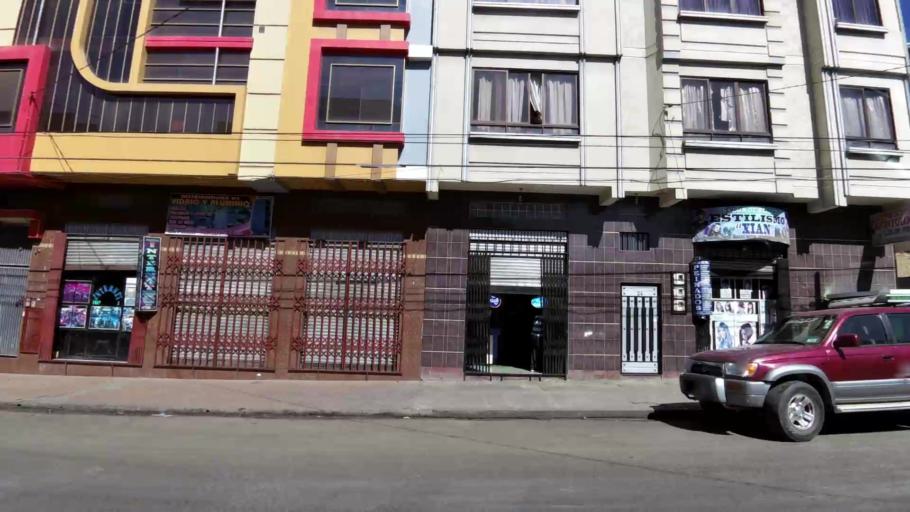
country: BO
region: La Paz
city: La Paz
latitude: -16.5129
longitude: -68.1572
